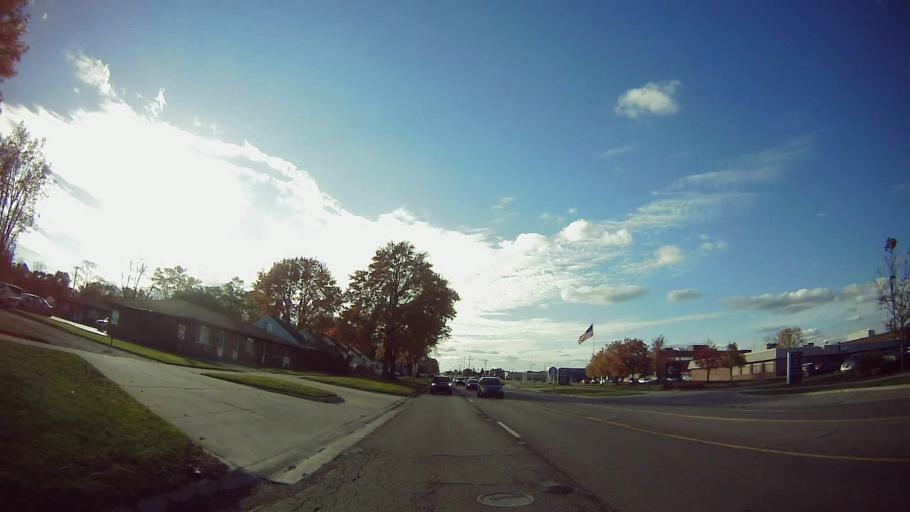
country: US
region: Michigan
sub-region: Oakland County
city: Clawson
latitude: 42.5481
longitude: -83.1504
